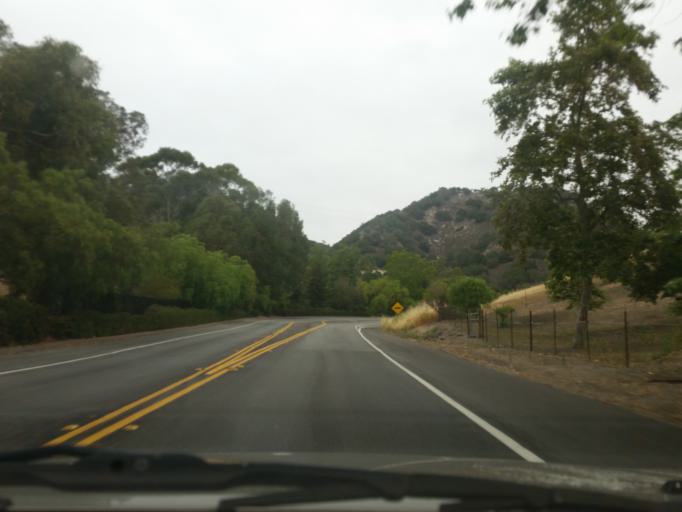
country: US
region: California
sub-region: San Luis Obispo County
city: Avila Beach
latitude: 35.1918
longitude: -120.7182
